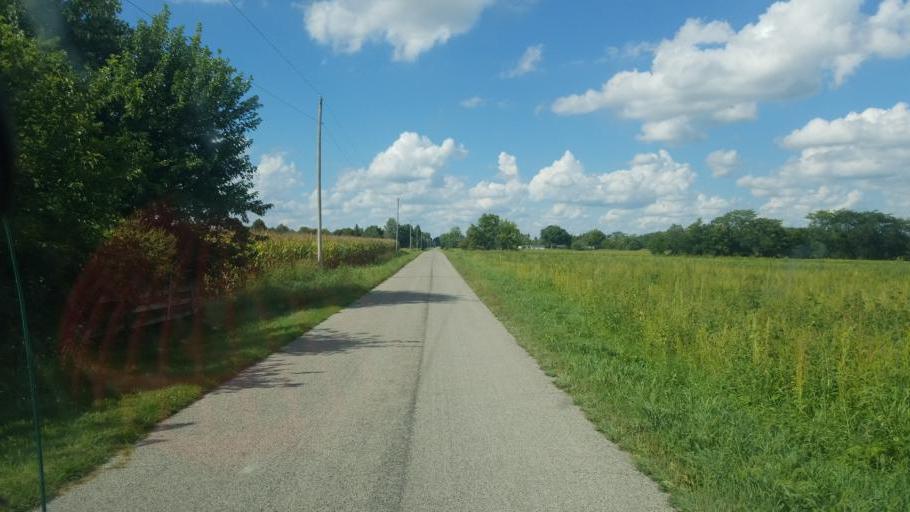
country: US
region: Ohio
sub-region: Union County
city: Richwood
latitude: 40.4692
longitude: -83.3272
